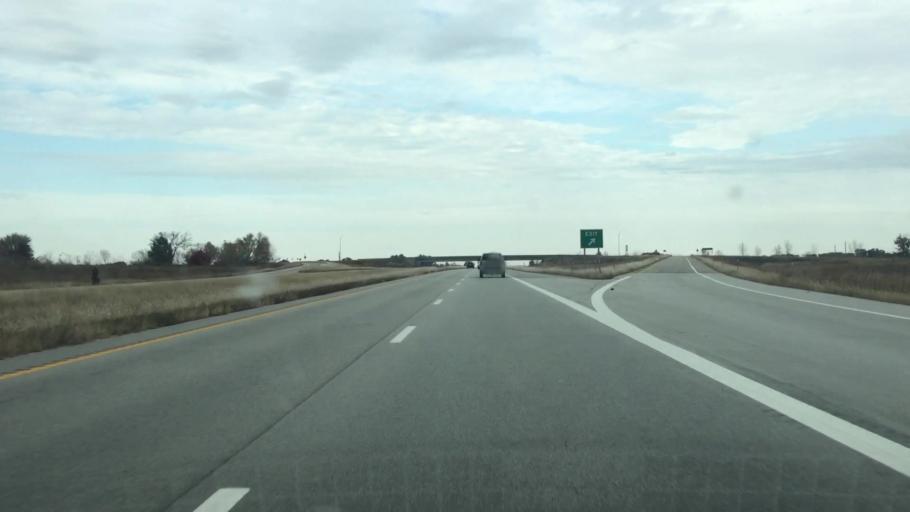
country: US
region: Missouri
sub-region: Henry County
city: Clinton
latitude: 38.2456
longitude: -93.7618
